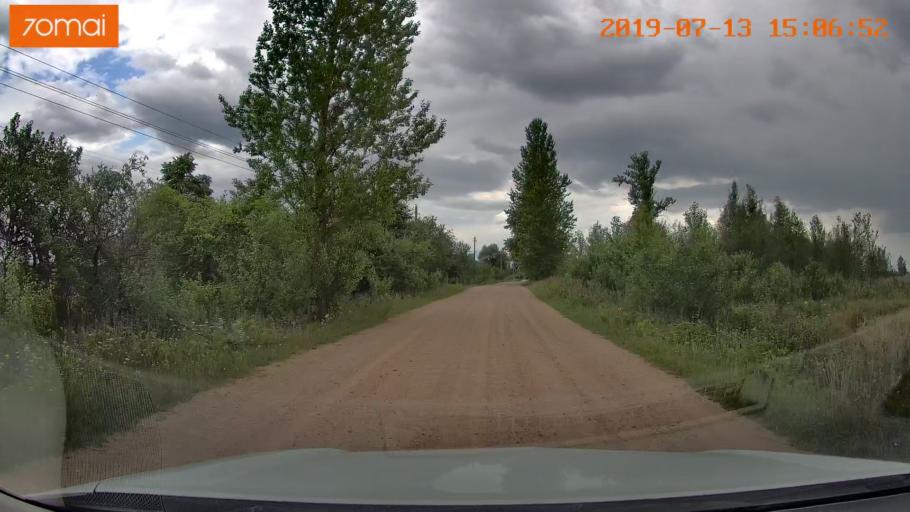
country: BY
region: Mogilev
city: Hlusha
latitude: 53.1953
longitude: 28.7563
